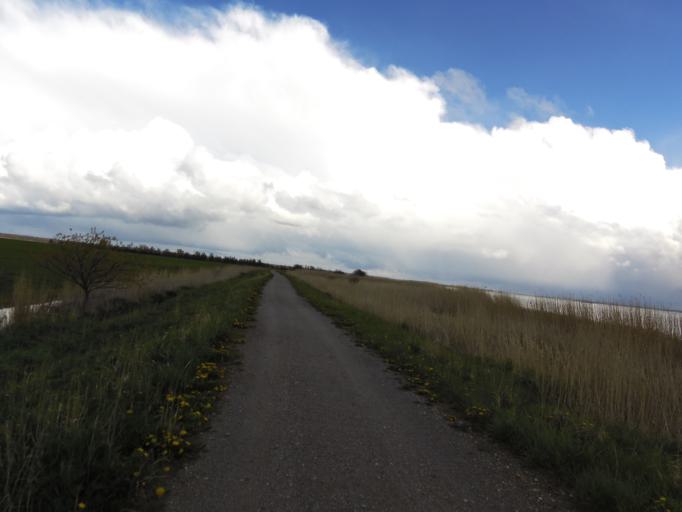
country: DE
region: Mecklenburg-Vorpommern
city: Born
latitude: 54.3794
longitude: 12.4437
